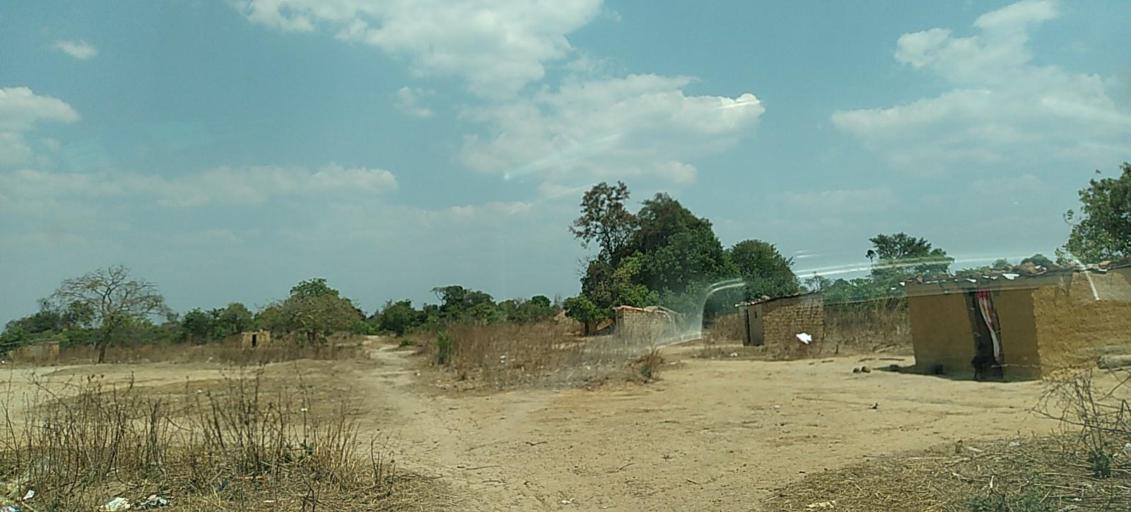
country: CD
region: Katanga
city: Kipushi
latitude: -11.9978
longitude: 27.4208
